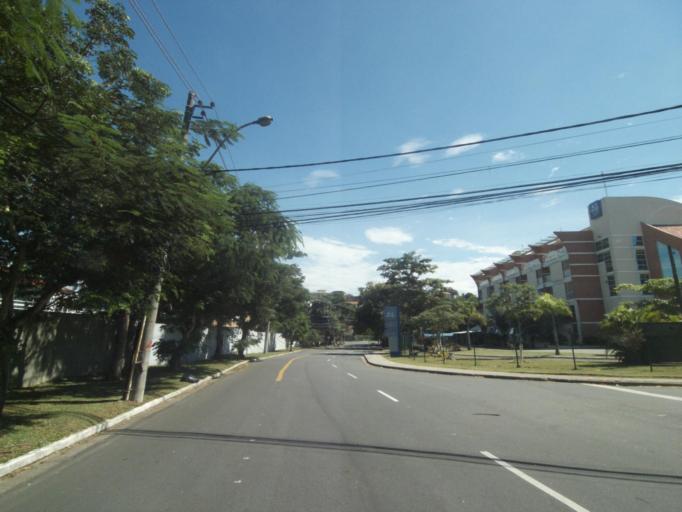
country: BR
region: Rio de Janeiro
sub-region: Niteroi
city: Niteroi
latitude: -22.9541
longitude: -43.0586
